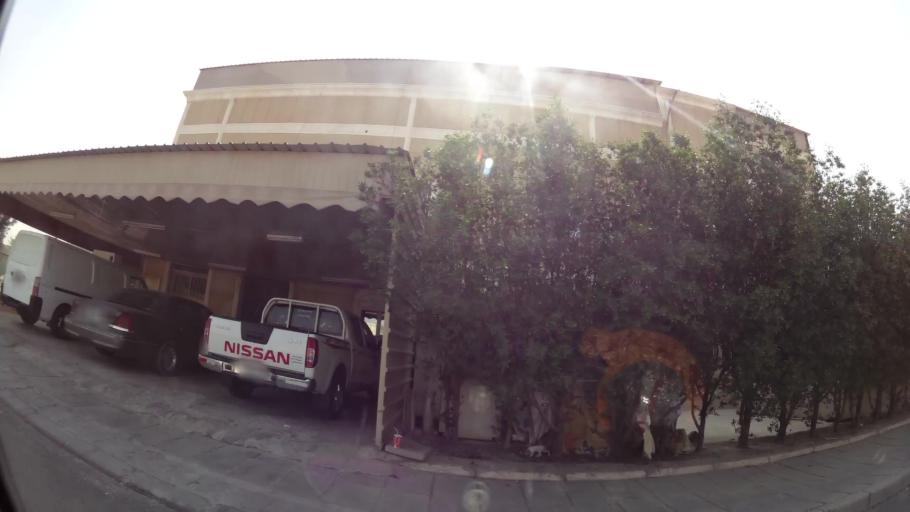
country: KW
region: Muhafazat al Jahra'
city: Al Jahra'
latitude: 29.3328
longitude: 47.6605
